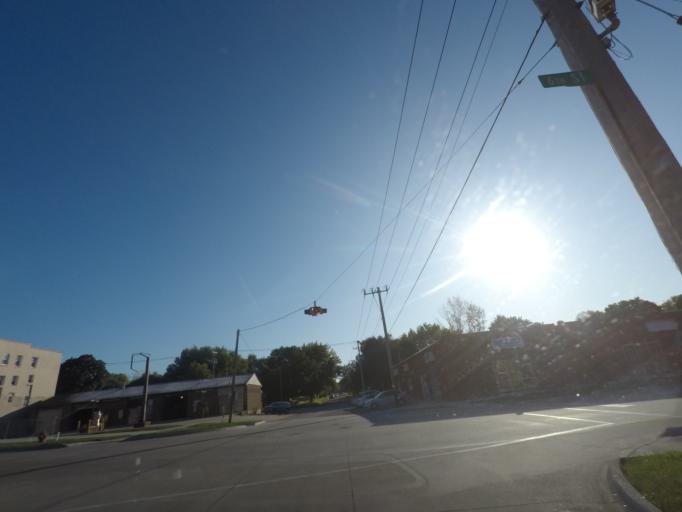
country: US
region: Iowa
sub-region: Story County
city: Nevada
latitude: 42.0196
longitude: -93.4525
